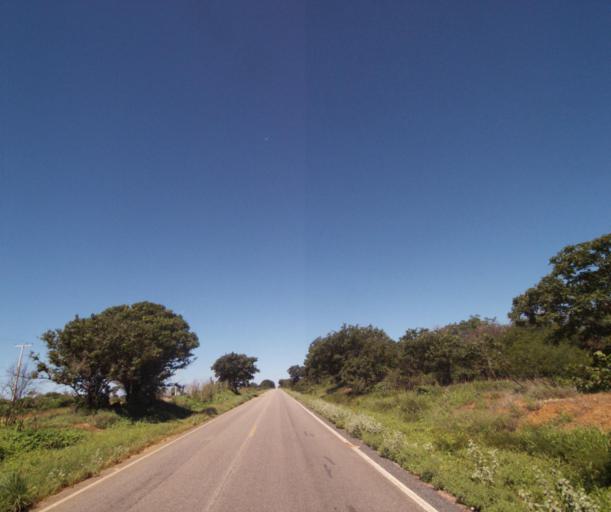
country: BR
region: Bahia
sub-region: Palmas De Monte Alto
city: Palmas de Monte Alto
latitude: -14.2604
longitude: -43.2971
